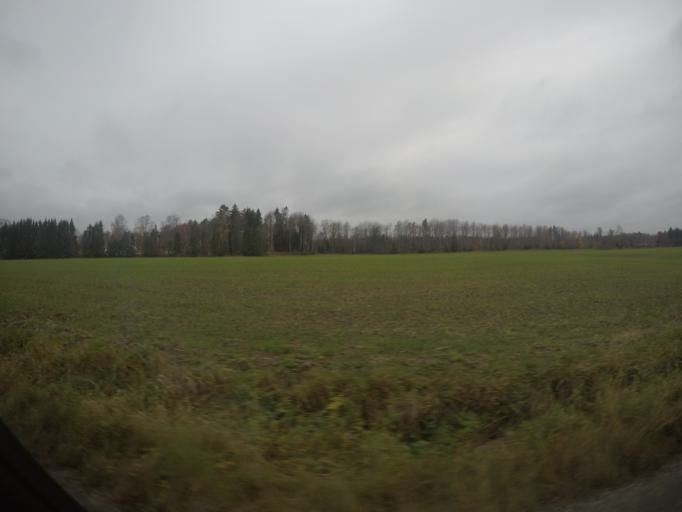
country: SE
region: Vaestmanland
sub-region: Vasteras
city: Skultuna
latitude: 59.7215
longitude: 16.4137
